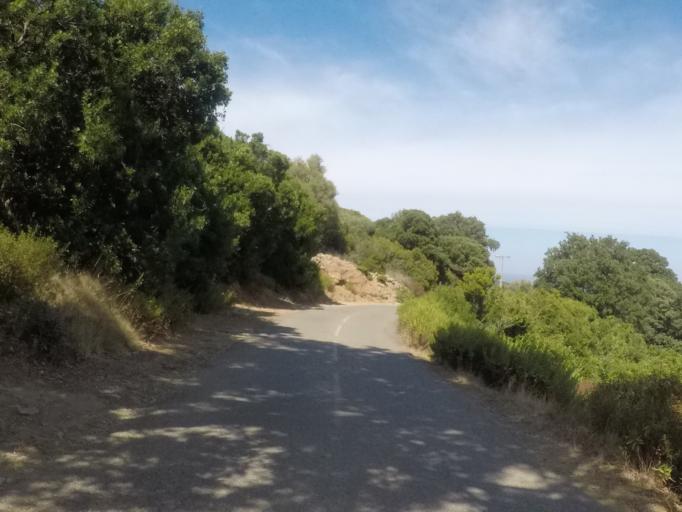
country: FR
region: Corsica
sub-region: Departement de la Haute-Corse
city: Brando
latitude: 42.9897
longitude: 9.4020
